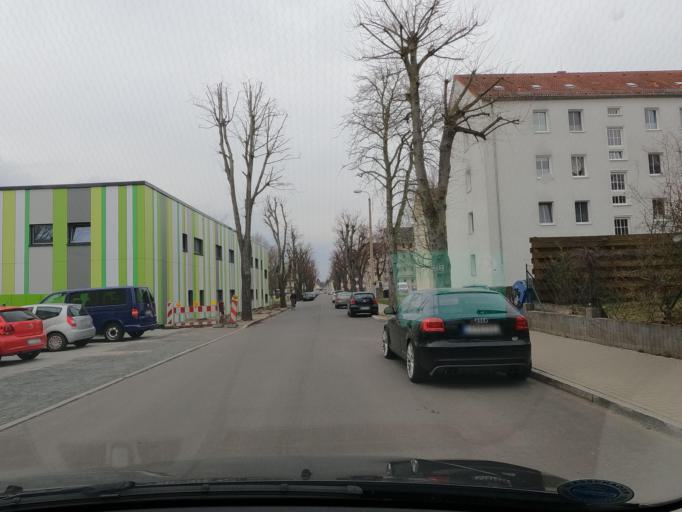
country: DE
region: Saxony
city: Schkeuditz
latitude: 51.3999
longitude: 12.2256
